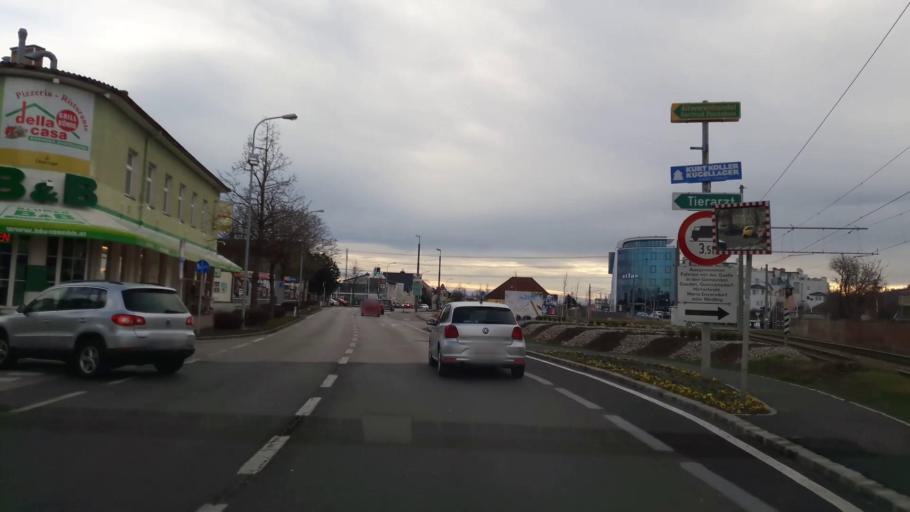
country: AT
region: Lower Austria
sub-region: Politischer Bezirk Modling
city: Wiener Neudorf
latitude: 48.0832
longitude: 16.3139
